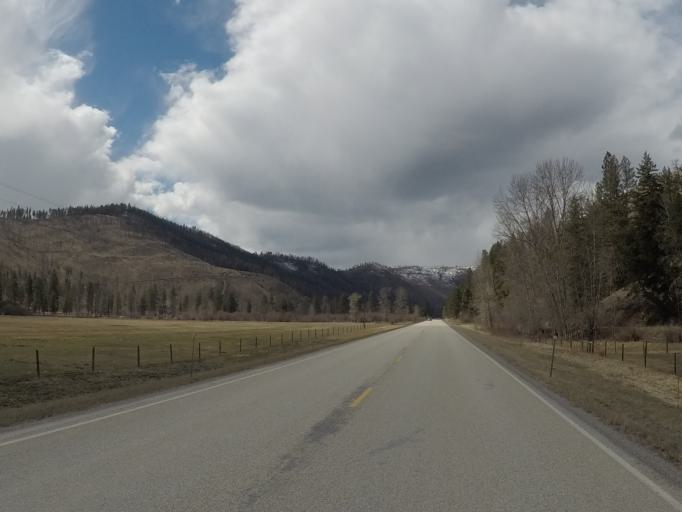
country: US
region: Montana
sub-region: Missoula County
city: Lolo
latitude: 46.7632
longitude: -114.2847
